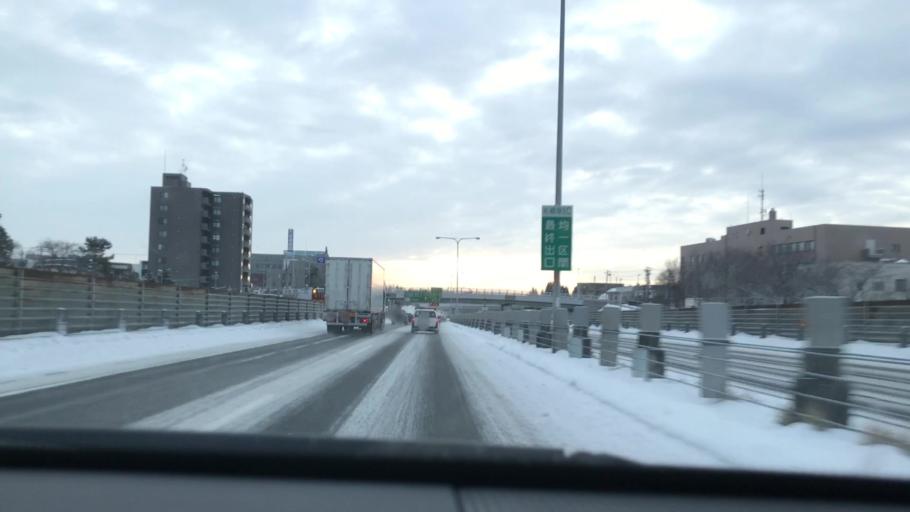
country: JP
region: Hokkaido
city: Sapporo
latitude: 43.0243
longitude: 141.4537
